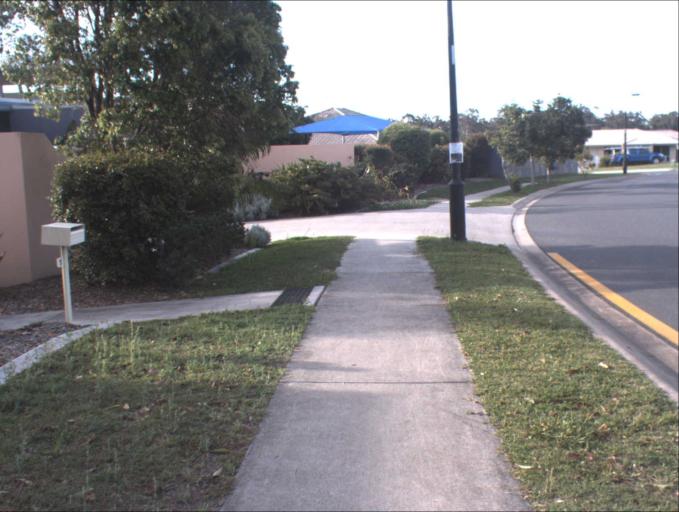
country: AU
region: Queensland
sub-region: Logan
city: Logan Reserve
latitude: -27.6996
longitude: 153.0982
